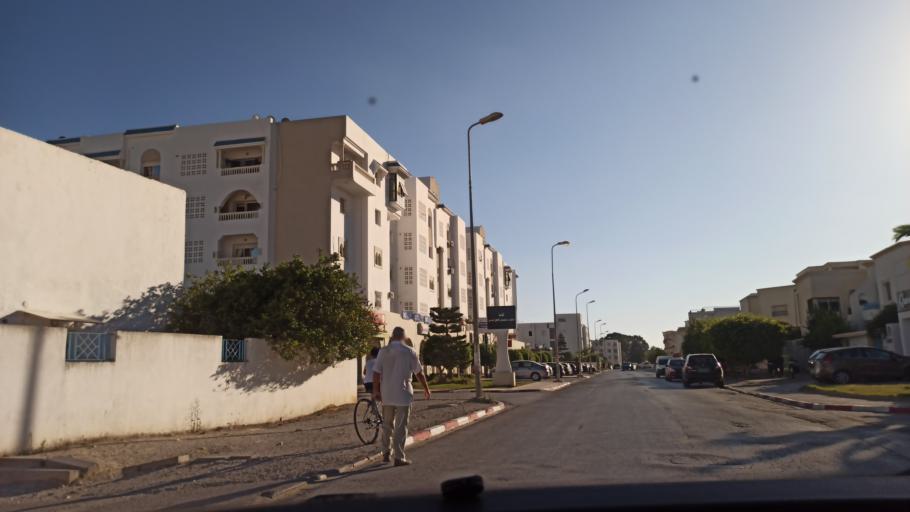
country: TN
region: Tunis
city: La Goulette
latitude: 36.8526
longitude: 10.2560
